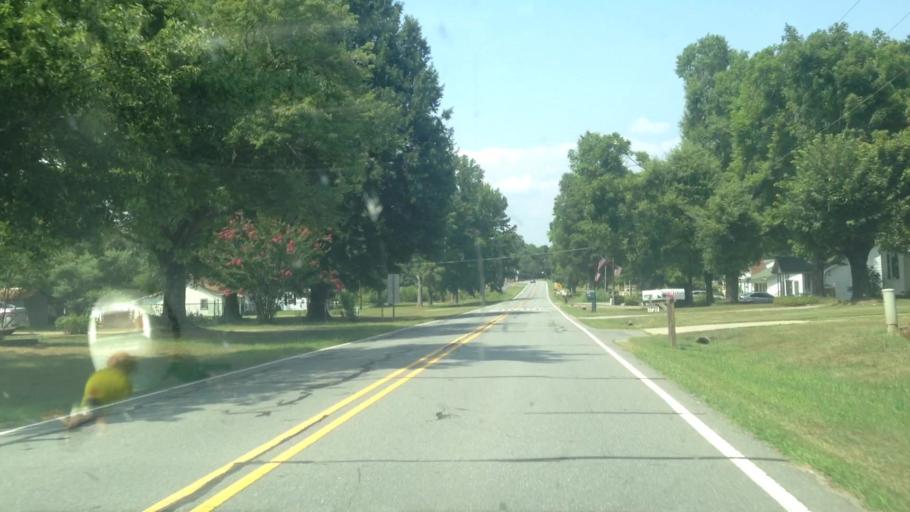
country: US
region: North Carolina
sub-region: Stokes County
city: Walnut Cove
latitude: 36.3258
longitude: -80.0489
